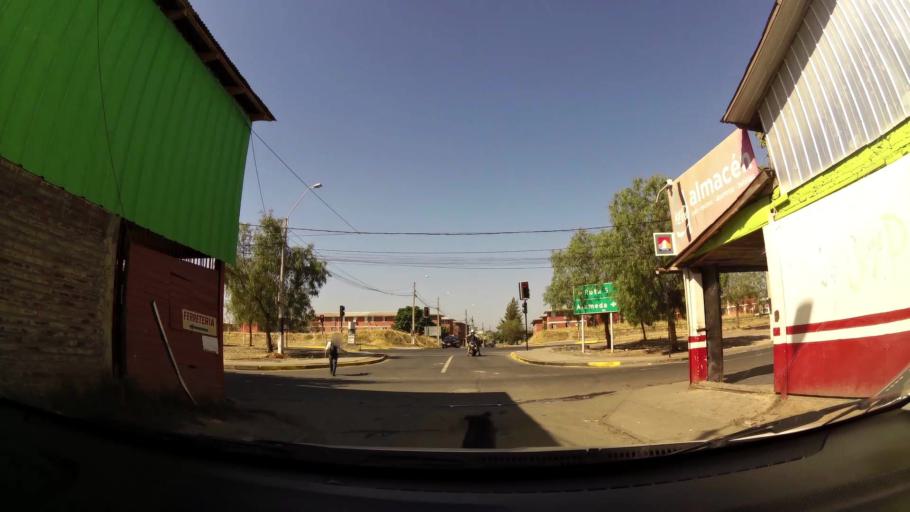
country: CL
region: Maule
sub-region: Provincia de Talca
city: Talca
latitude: -35.3974
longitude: -71.6471
